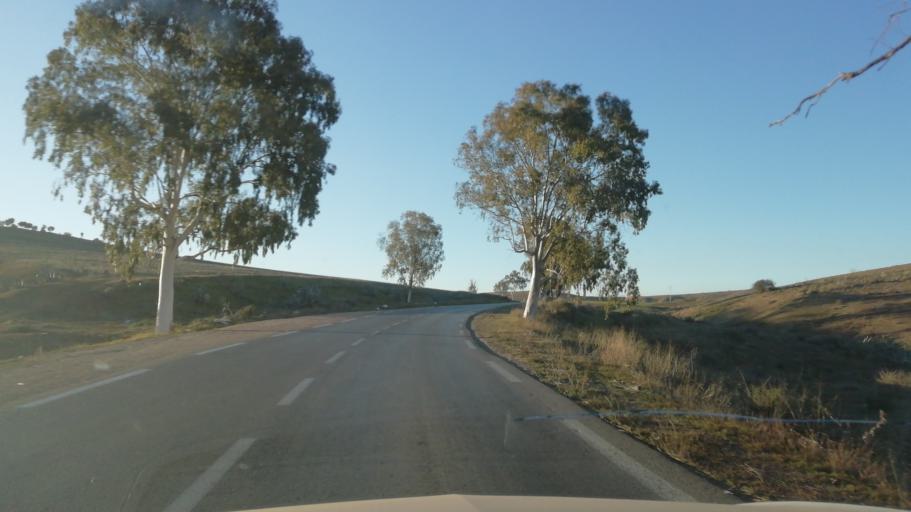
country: DZ
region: Tlemcen
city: Nedroma
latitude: 34.8286
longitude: -1.6632
